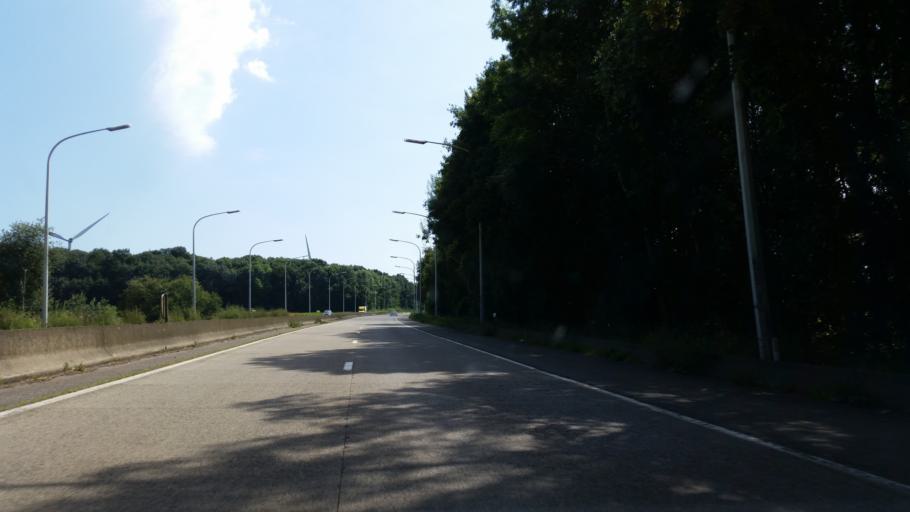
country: BE
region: Wallonia
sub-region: Province de Namur
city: Hamois
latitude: 50.3021
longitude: 5.1658
